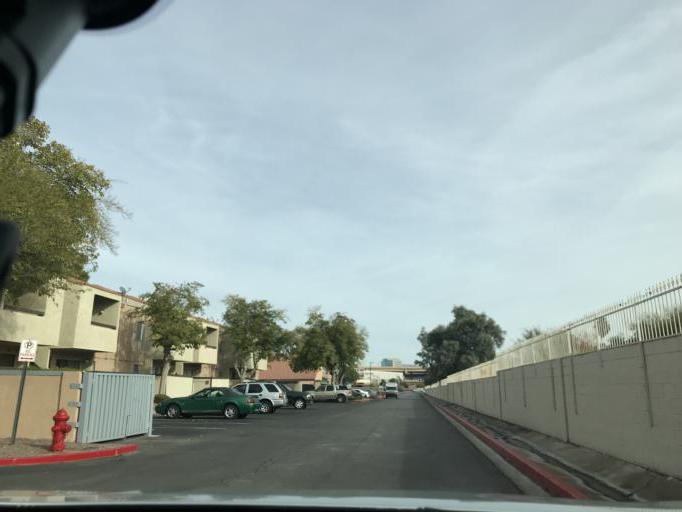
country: US
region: Nevada
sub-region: Clark County
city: Las Vegas
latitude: 36.1734
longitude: -115.1639
